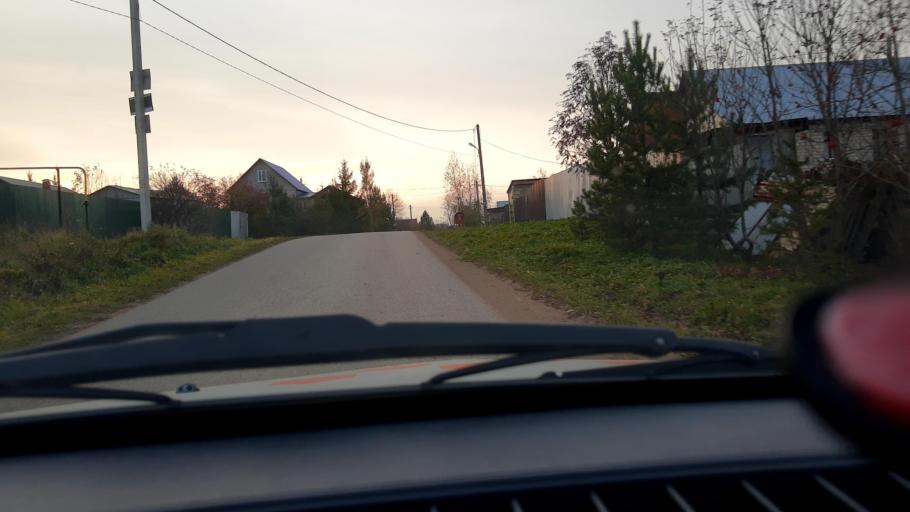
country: RU
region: Bashkortostan
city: Iglino
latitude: 54.7925
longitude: 56.3241
